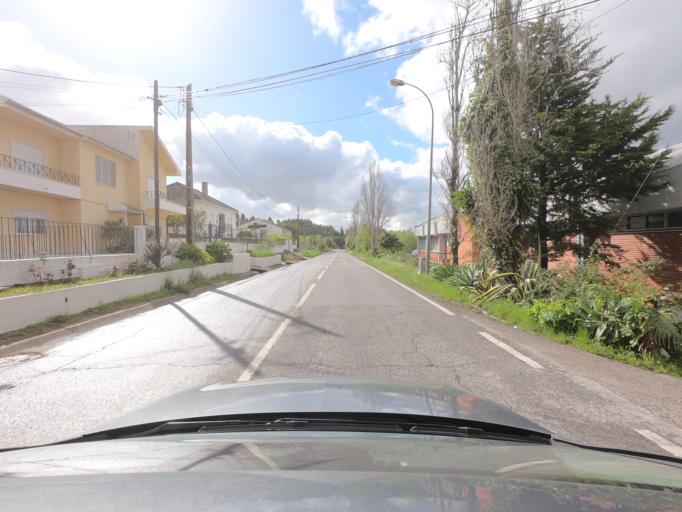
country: PT
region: Lisbon
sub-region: Oeiras
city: Quejas
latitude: 38.7305
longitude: -9.2583
